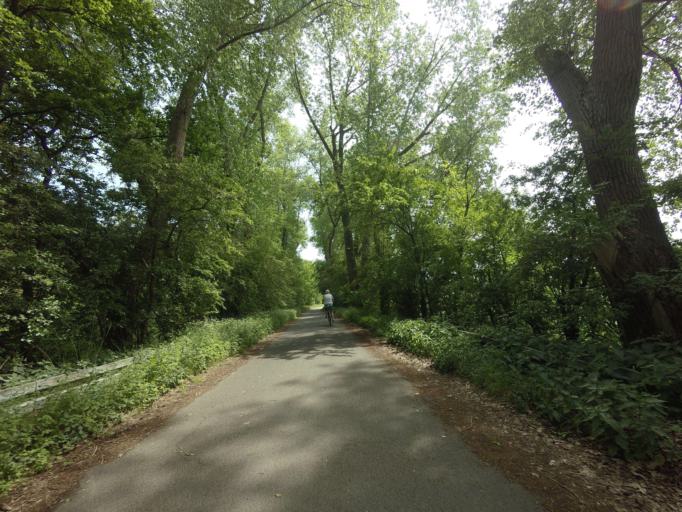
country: DE
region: Lower Saxony
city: Klein Schwulper
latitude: 52.3128
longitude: 10.4729
